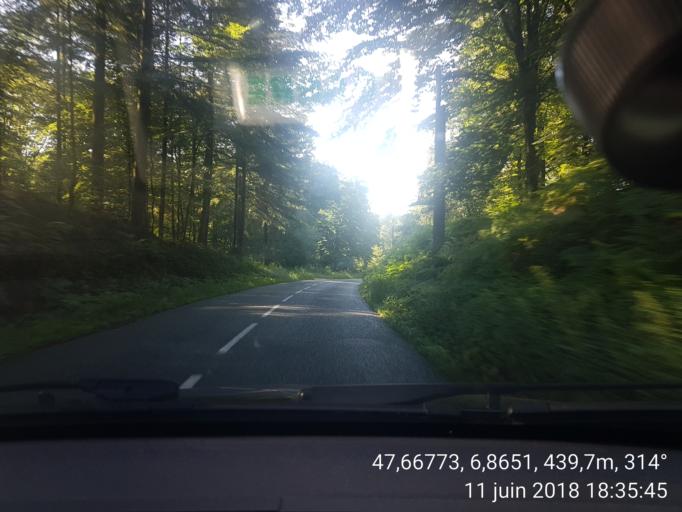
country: FR
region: Franche-Comte
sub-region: Territoire de Belfort
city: Offemont
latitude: 47.6675
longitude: 6.8653
